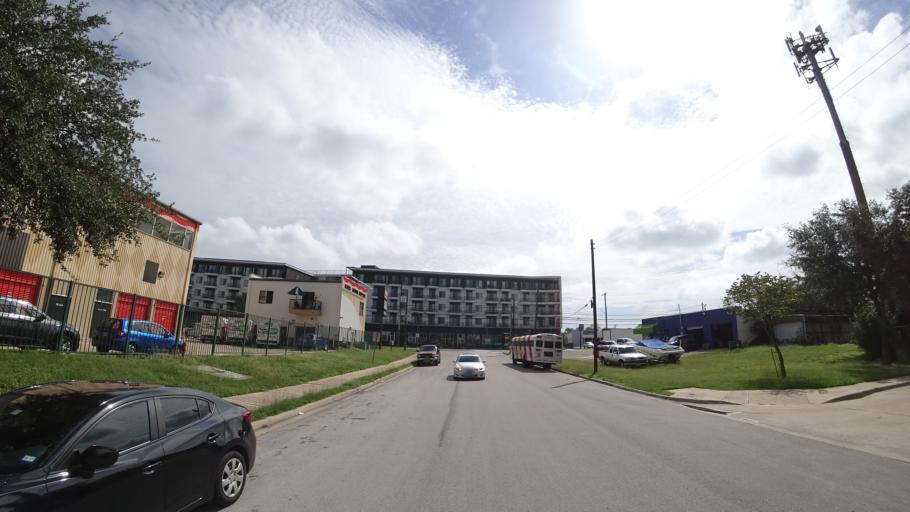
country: US
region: Texas
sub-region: Travis County
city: Austin
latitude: 30.3422
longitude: -97.7394
